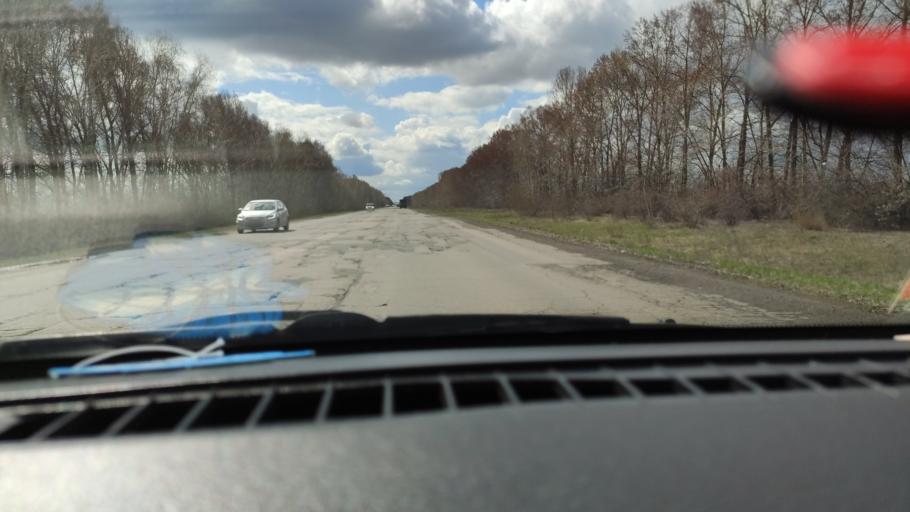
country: RU
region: Samara
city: Tol'yatti
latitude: 53.6403
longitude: 49.4200
